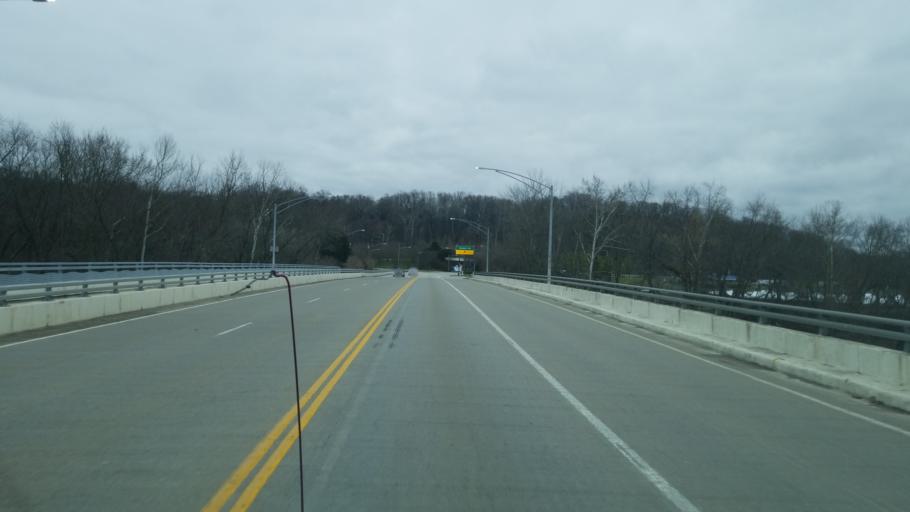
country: US
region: Kentucky
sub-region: Campbell County
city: Fort Thomas
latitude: 39.0858
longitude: -84.4216
